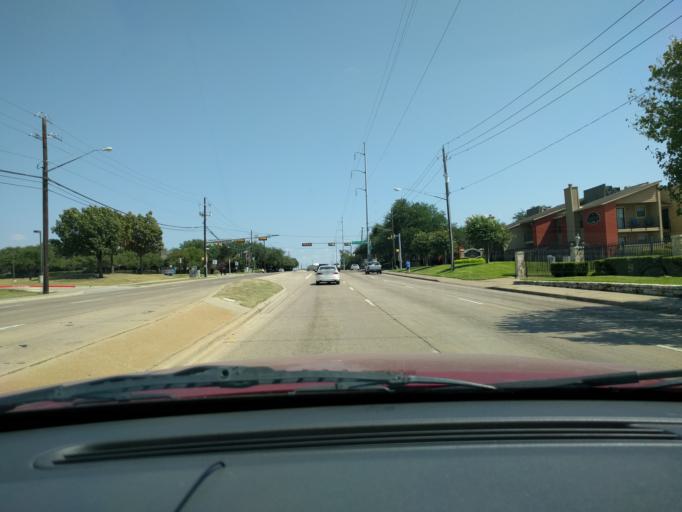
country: US
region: Texas
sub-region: Dallas County
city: Richardson
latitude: 32.9095
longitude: -96.7245
